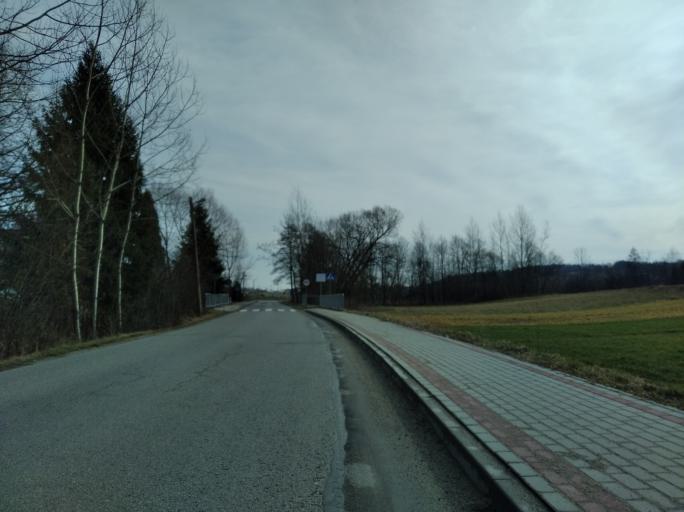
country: PL
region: Subcarpathian Voivodeship
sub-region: Powiat brzozowski
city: Orzechowka
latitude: 49.7268
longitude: 21.9488
